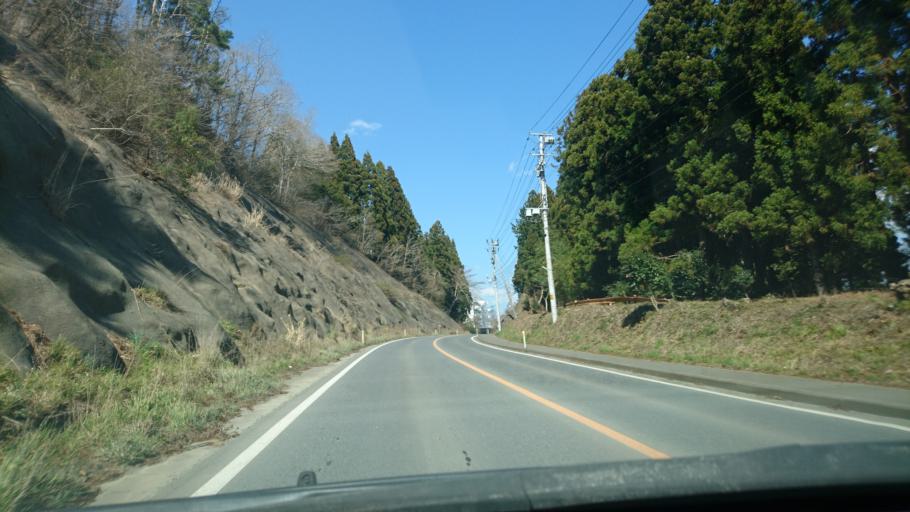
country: JP
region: Miyagi
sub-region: Oshika Gun
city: Onagawa Cho
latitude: 38.6557
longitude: 141.4472
